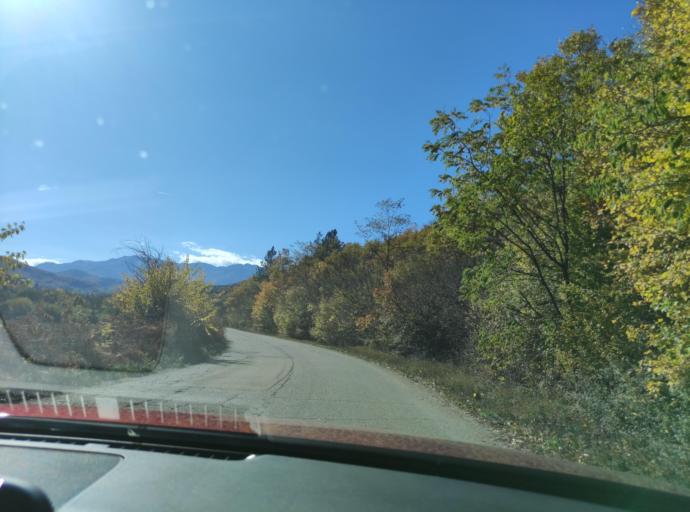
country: BG
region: Montana
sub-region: Obshtina Chiprovtsi
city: Chiprovtsi
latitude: 43.4000
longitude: 22.9296
